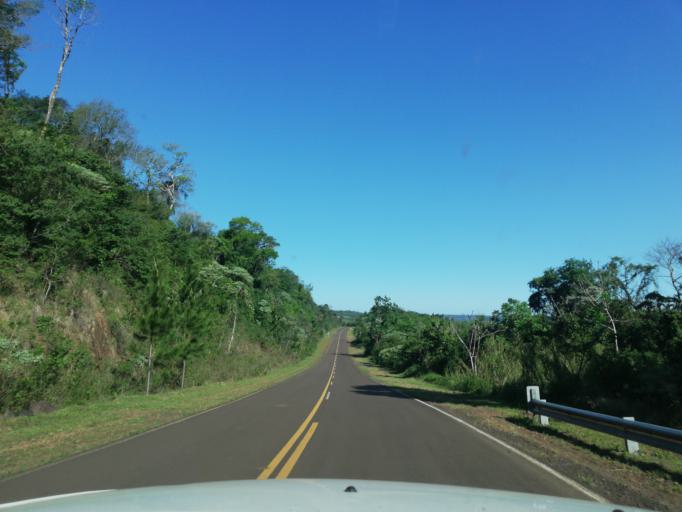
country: AR
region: Misiones
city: Arroyo del Medio
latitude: -27.6555
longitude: -55.4027
